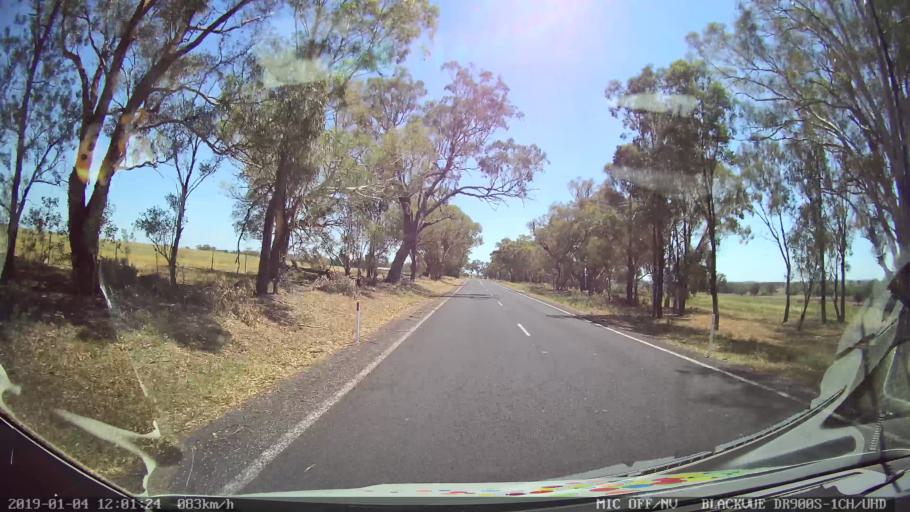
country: AU
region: New South Wales
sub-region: Wellington
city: Wellington
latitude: -32.7912
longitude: 148.6894
